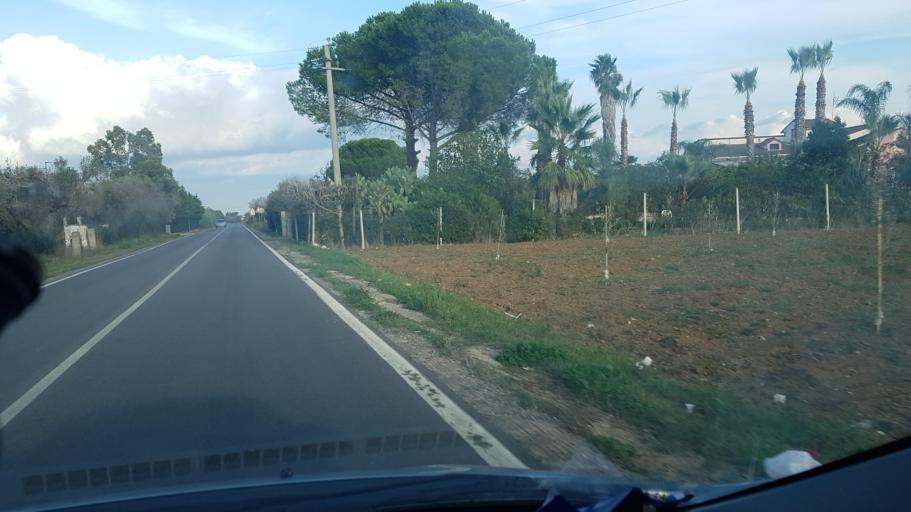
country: IT
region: Apulia
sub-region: Provincia di Lecce
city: Veglie
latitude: 40.3369
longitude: 17.9894
